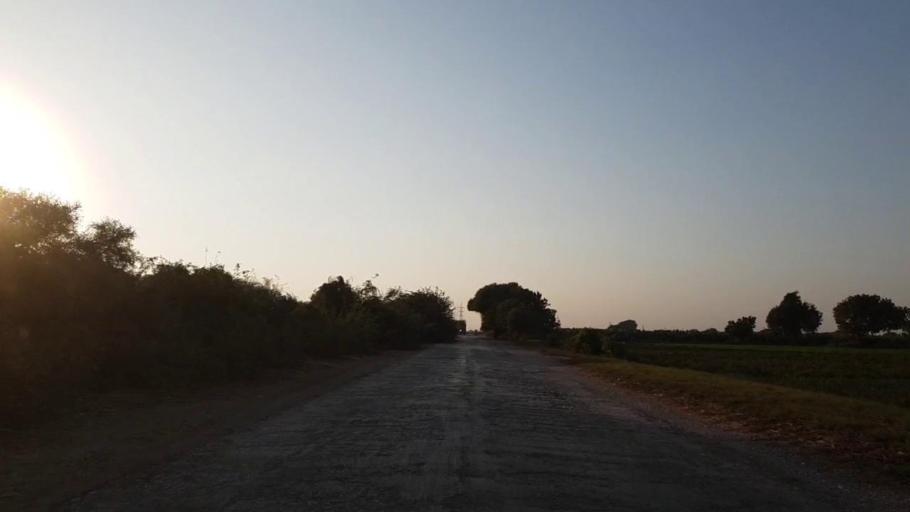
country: PK
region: Sindh
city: Chambar
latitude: 25.2219
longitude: 68.7253
